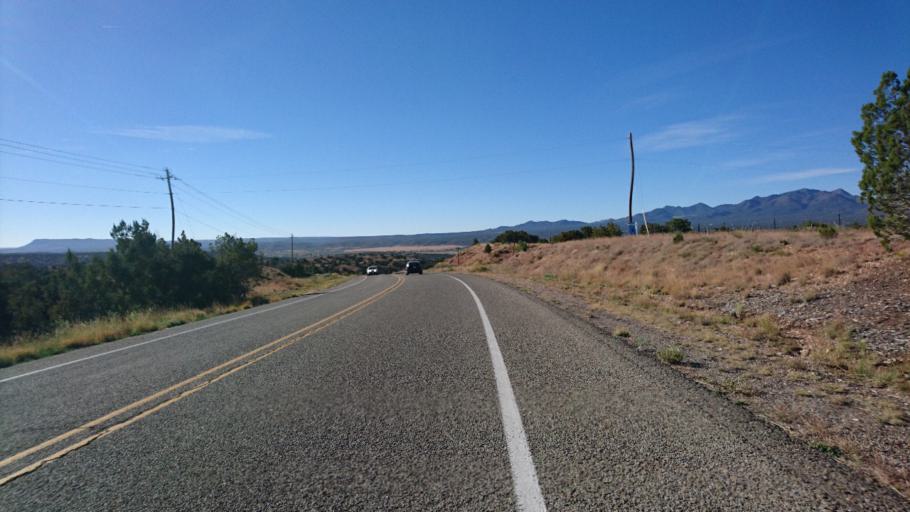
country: US
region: New Mexico
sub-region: Santa Fe County
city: La Cienega
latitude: 35.4491
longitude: -106.0778
